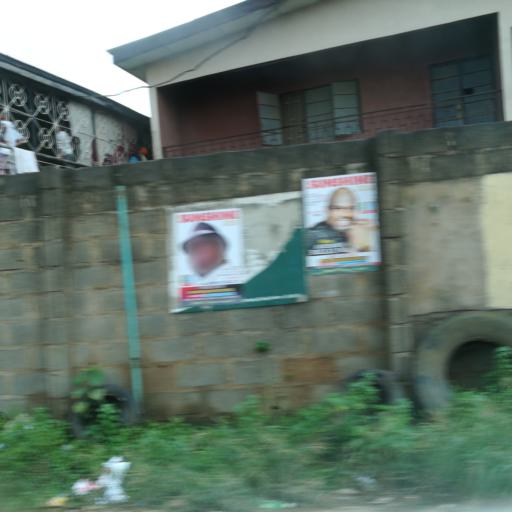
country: NG
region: Lagos
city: Agege
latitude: 6.6089
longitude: 3.2980
